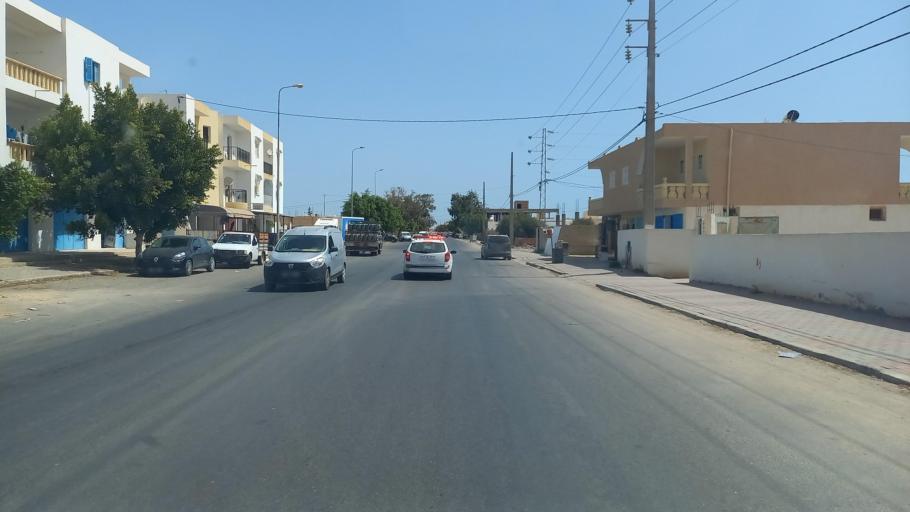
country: TN
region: Madanin
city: Zarzis
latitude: 33.4942
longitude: 11.0810
